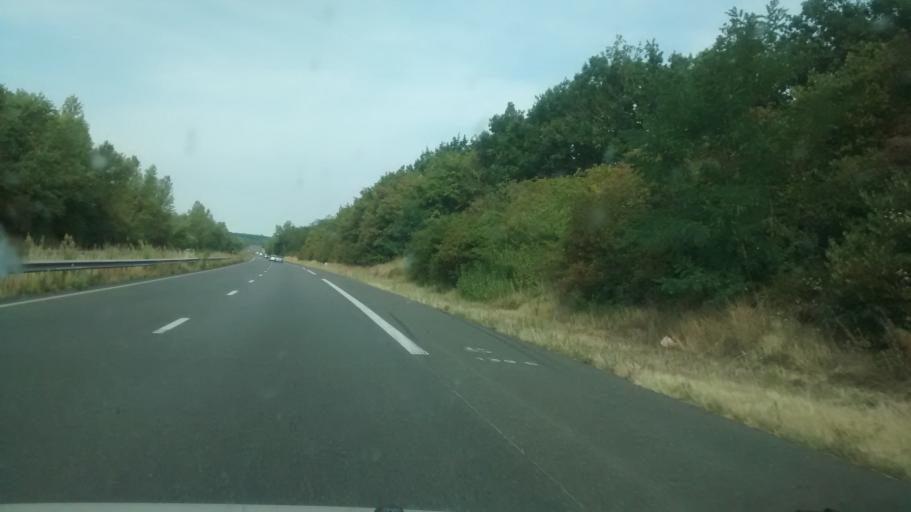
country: FR
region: Midi-Pyrenees
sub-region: Departement du Tarn-et-Garonne
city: Lamagistere
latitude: 44.1034
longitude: 0.7671
